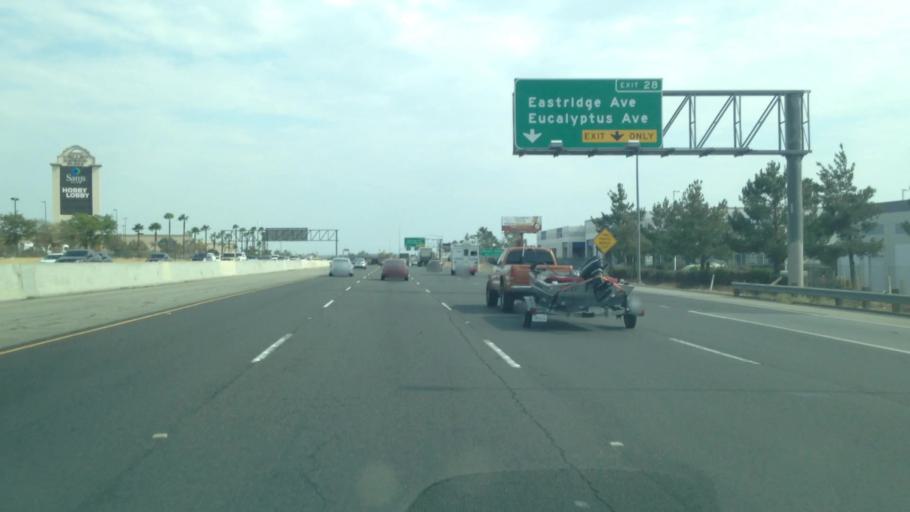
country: US
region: California
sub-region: Riverside County
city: March Air Force Base
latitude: 33.9388
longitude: -117.2912
